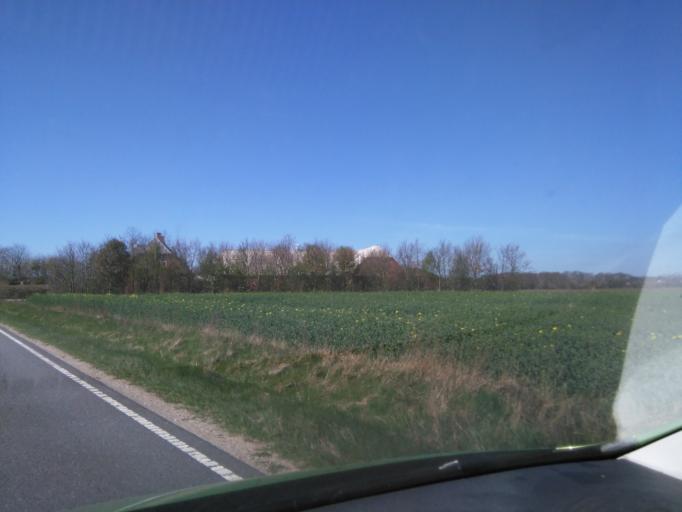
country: DK
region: South Denmark
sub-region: Varde Kommune
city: Varde
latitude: 55.6263
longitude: 8.3955
